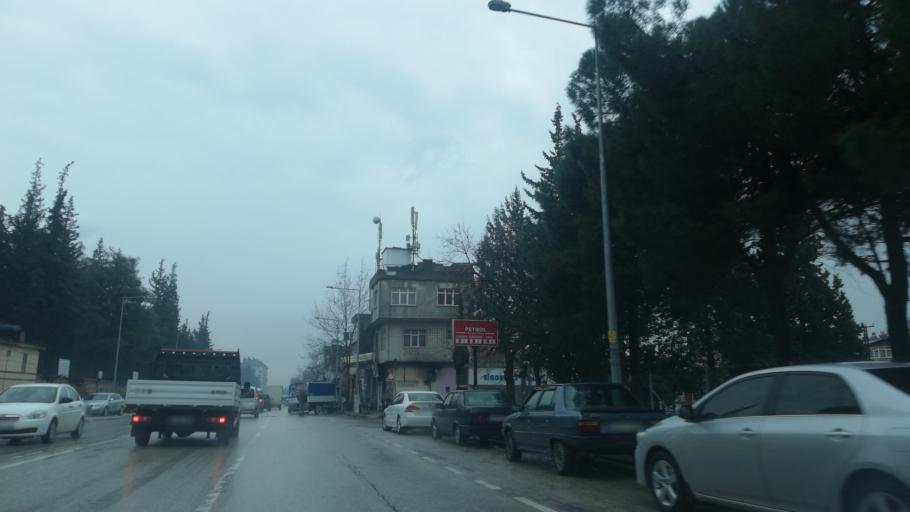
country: TR
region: Kahramanmaras
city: Kahramanmaras
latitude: 37.5755
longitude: 36.9359
